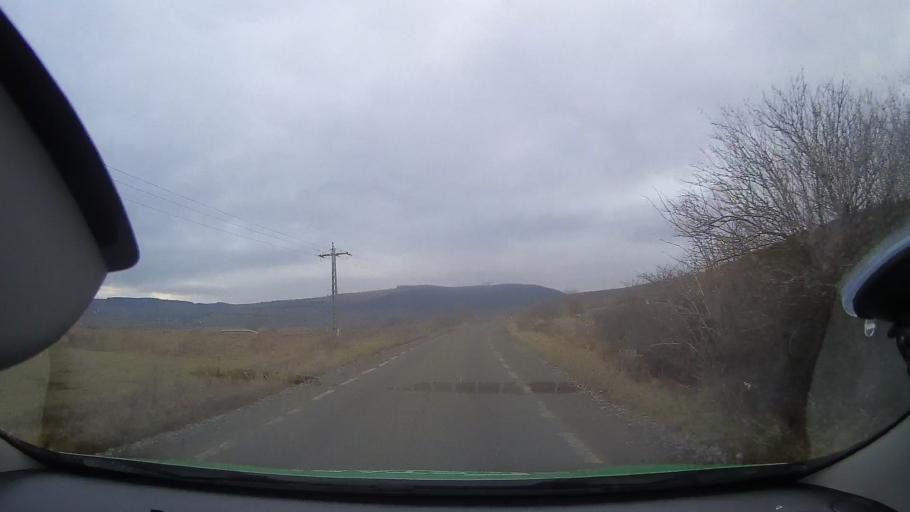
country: RO
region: Mures
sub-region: Comuna Atintis
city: Atintis
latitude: 46.4004
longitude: 24.0889
